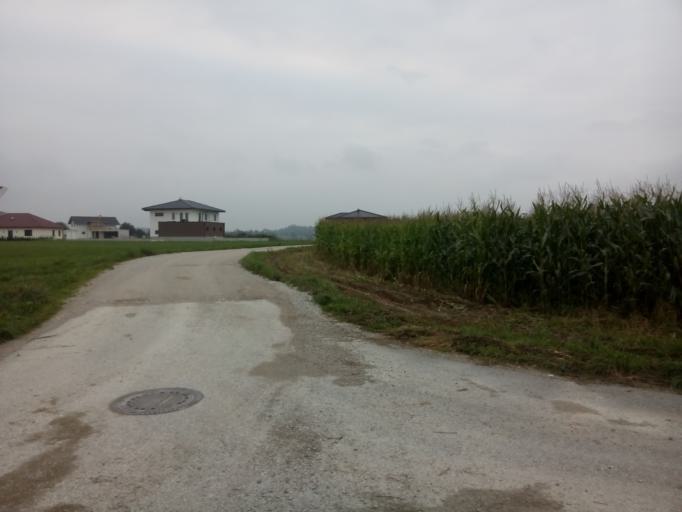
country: AT
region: Upper Austria
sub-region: Politischer Bezirk Gmunden
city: Vorchdorf
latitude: 48.0466
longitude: 13.9768
